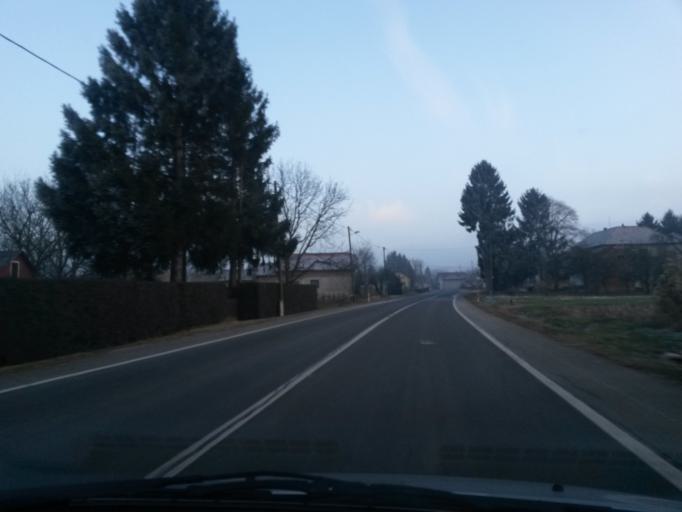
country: HR
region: Varazdinska
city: Ludbreg
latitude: 46.2241
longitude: 16.6732
